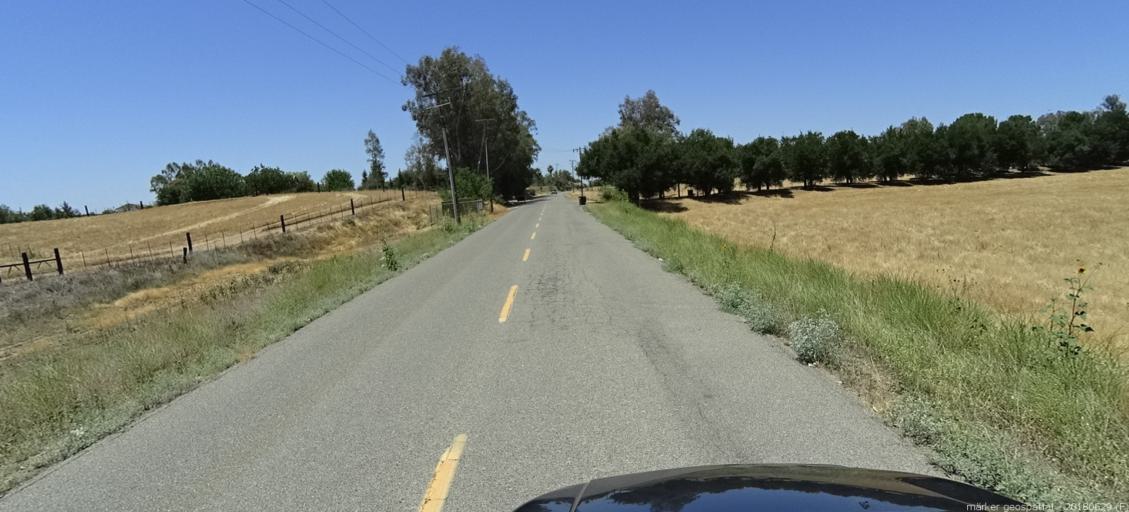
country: US
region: California
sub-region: Madera County
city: Parksdale
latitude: 37.0039
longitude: -119.9814
